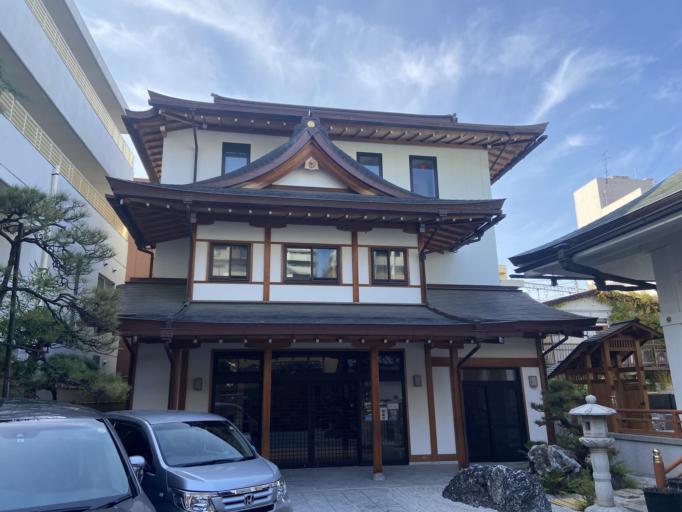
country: JP
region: Hyogo
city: Nishinomiya-hama
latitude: 34.7365
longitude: 135.3359
